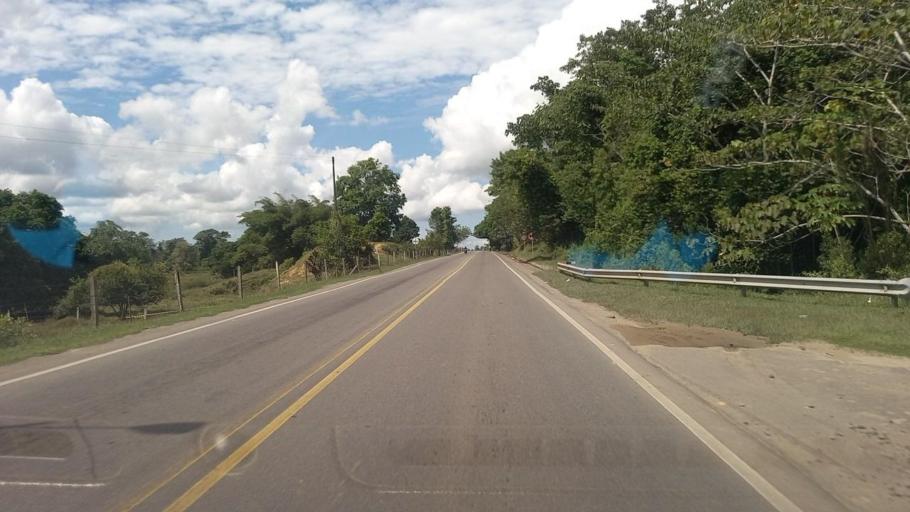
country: CO
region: Santander
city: Barrancabermeja
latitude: 7.1228
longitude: -73.5899
